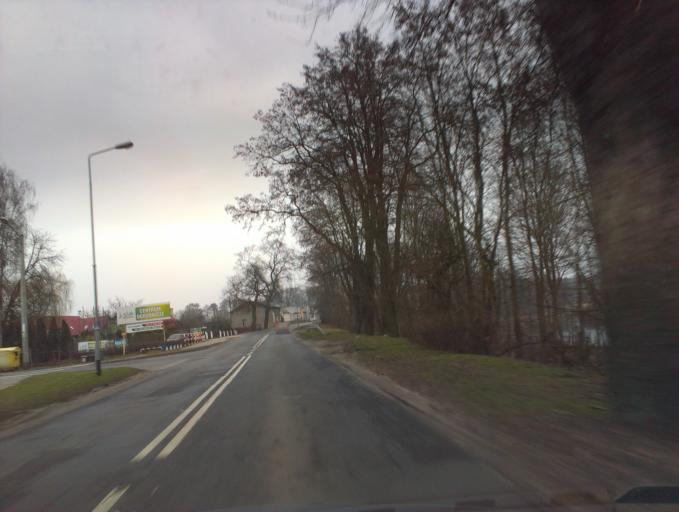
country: PL
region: Greater Poland Voivodeship
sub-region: Powiat pilski
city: Pila
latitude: 53.1697
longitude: 16.7394
